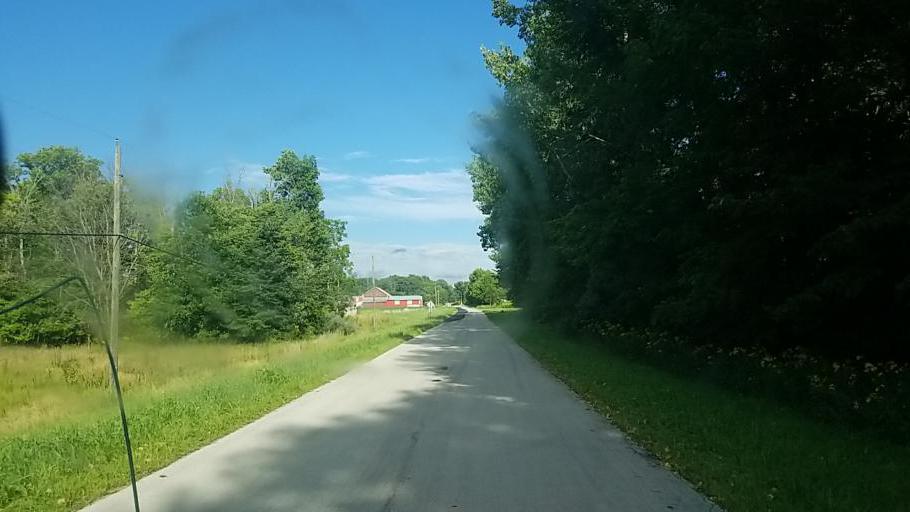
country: US
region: Ohio
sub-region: Wyandot County
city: Upper Sandusky
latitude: 40.7592
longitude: -83.3806
